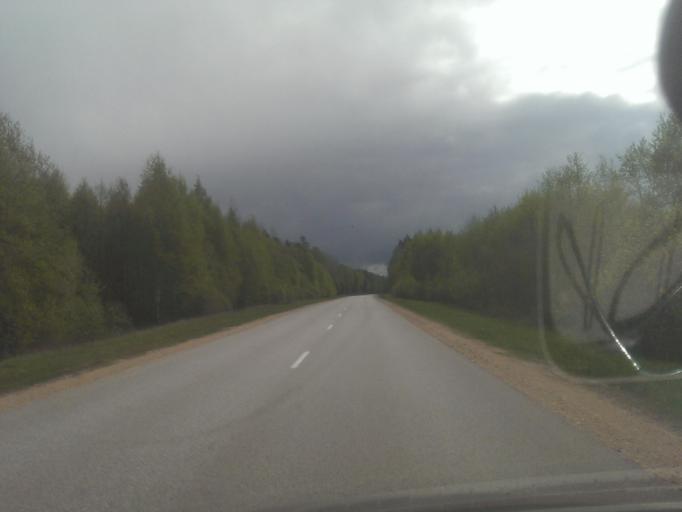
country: LV
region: Ventspils Rajons
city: Piltene
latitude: 57.1679
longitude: 21.6778
